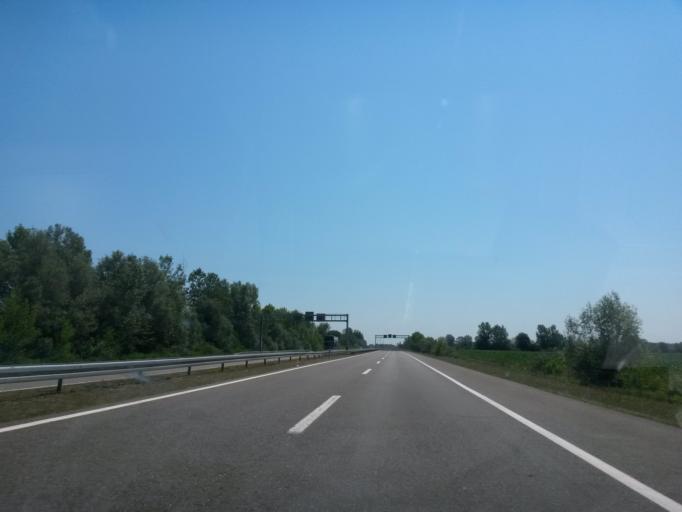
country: BA
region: Federation of Bosnia and Herzegovina
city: Donja Dubica
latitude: 45.1348
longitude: 18.3891
